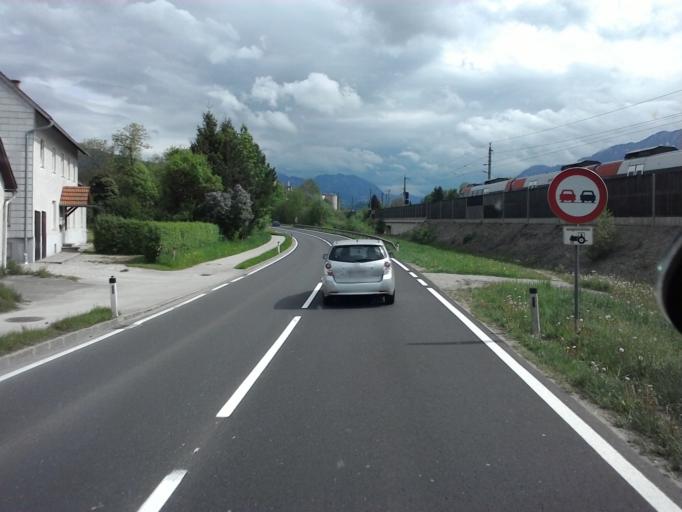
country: AT
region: Upper Austria
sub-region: Politischer Bezirk Kirchdorf an der Krems
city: Micheldorf in Oberoesterreich
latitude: 47.9146
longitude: 14.1109
